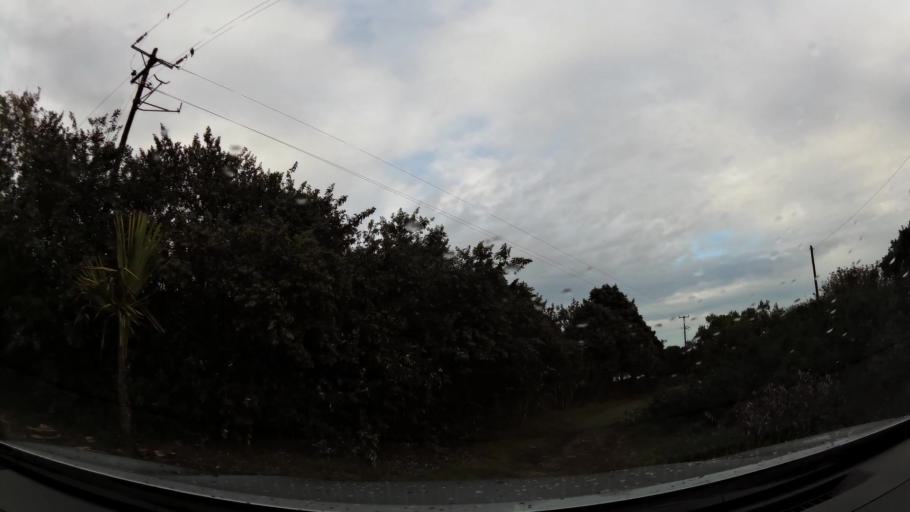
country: ZA
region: Eastern Cape
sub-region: Nelson Mandela Bay Metropolitan Municipality
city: Port Elizabeth
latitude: -34.0200
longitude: 25.5110
